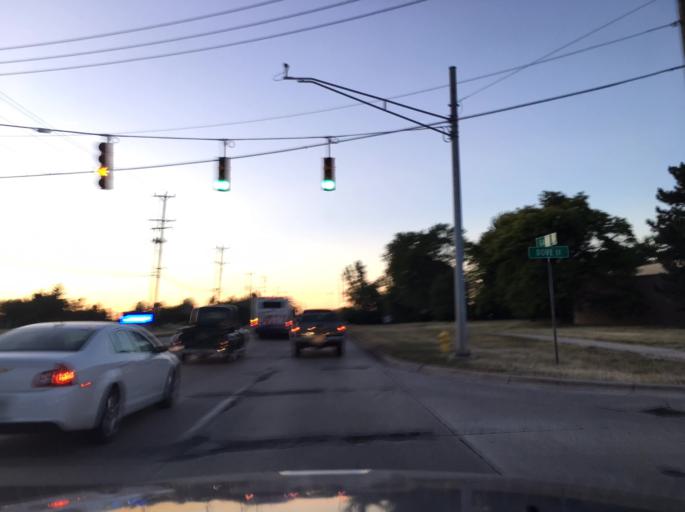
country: US
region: Michigan
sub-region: Macomb County
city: Clinton
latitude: 42.6222
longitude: -82.9532
